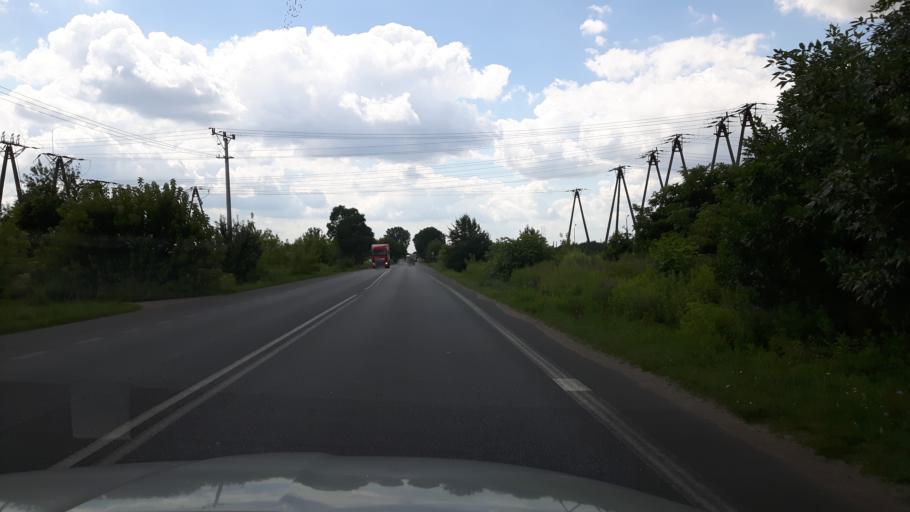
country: PL
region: Masovian Voivodeship
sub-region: Powiat wyszkowski
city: Wyszkow
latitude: 52.6194
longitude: 21.4919
